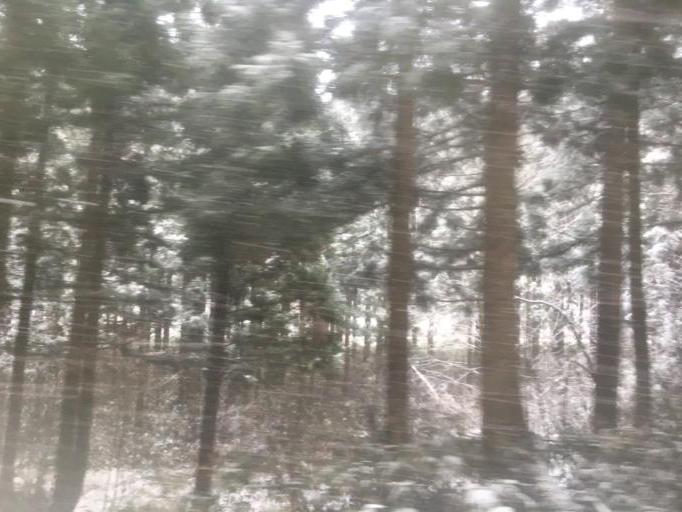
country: JP
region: Aomori
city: Goshogawara
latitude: 41.1154
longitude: 140.5272
